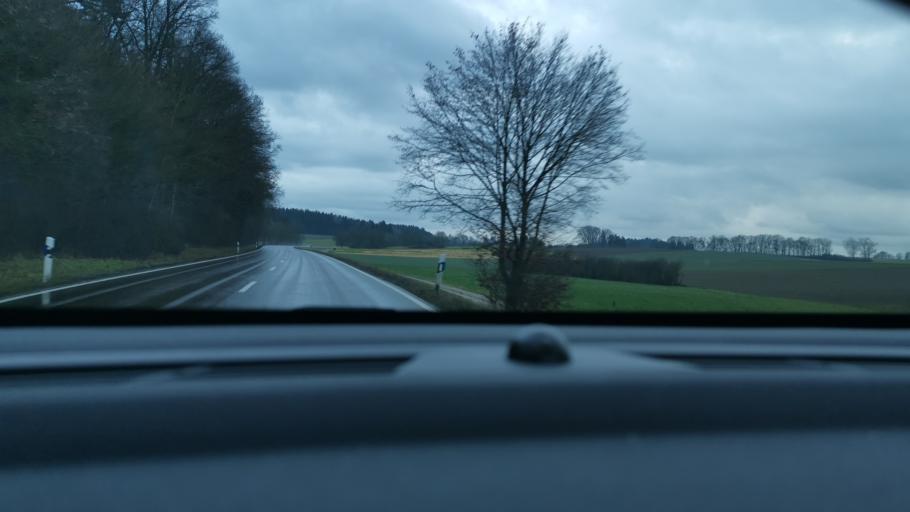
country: DE
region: Bavaria
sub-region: Swabia
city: Affing
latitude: 48.4871
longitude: 11.0081
